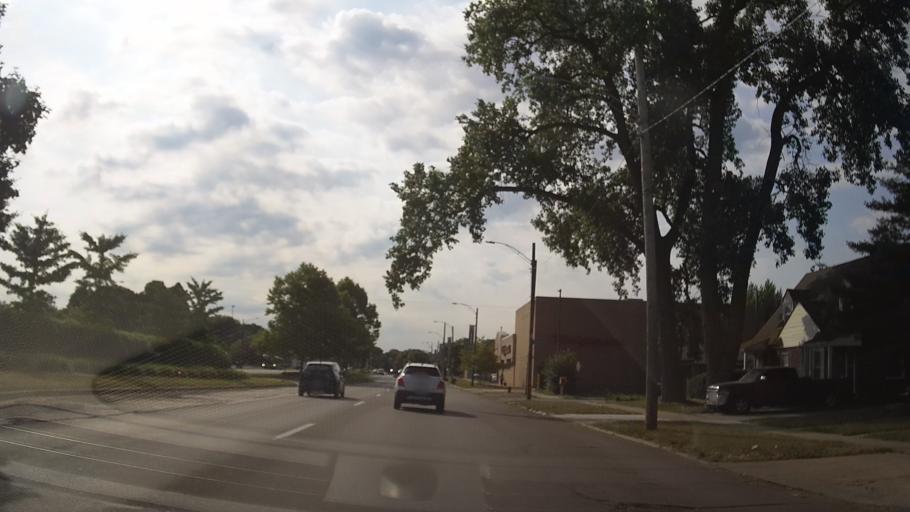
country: US
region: Michigan
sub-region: Wayne County
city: Harper Woods
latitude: 42.4180
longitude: -82.9134
